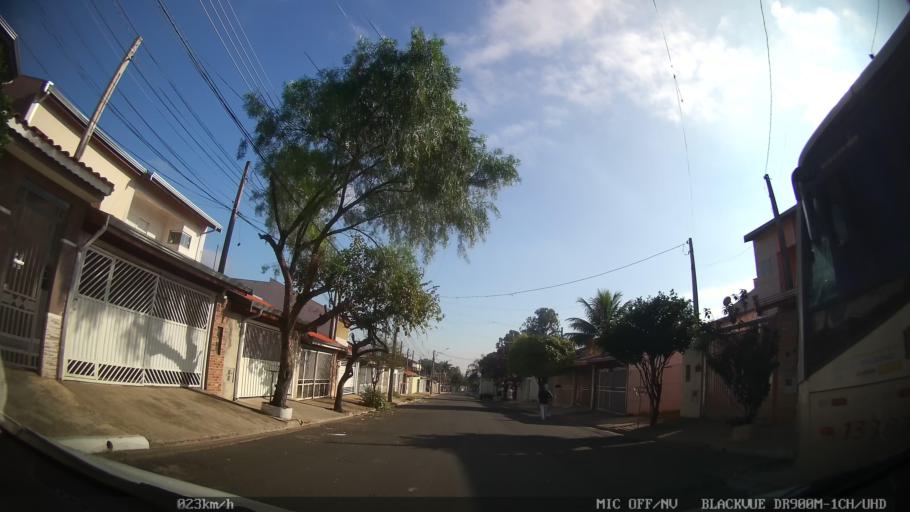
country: BR
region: Sao Paulo
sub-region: Hortolandia
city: Hortolandia
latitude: -22.9087
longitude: -47.1798
